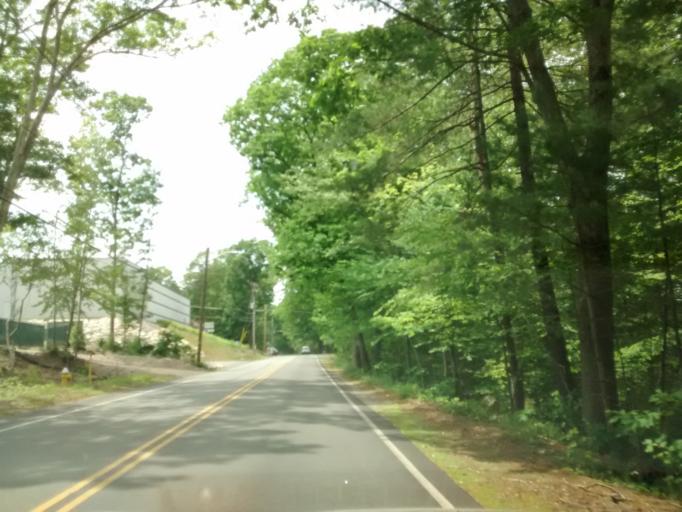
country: US
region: Massachusetts
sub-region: Worcester County
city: Whitinsville
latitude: 42.1083
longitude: -71.6742
